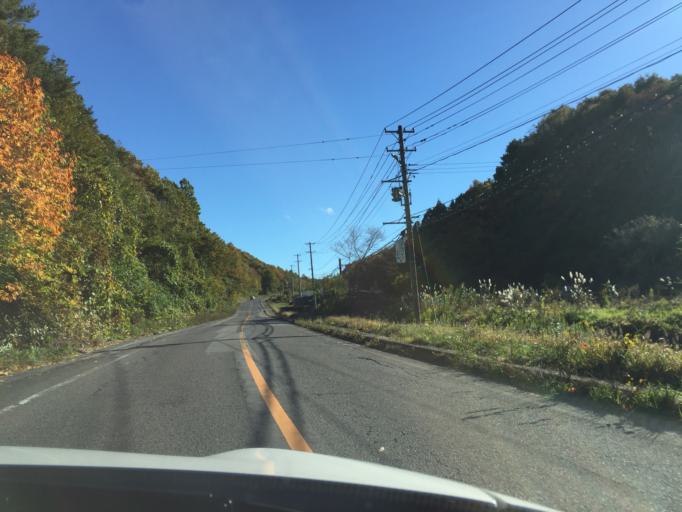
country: JP
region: Fukushima
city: Funehikimachi-funehiki
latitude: 37.2582
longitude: 140.6374
